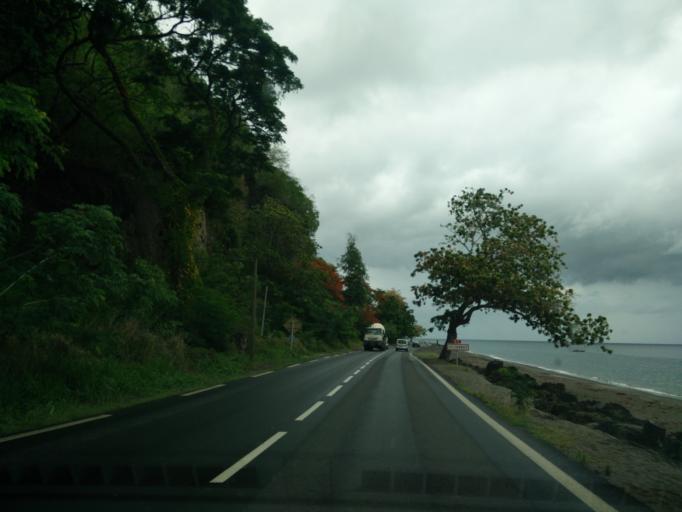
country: MQ
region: Martinique
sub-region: Martinique
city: Saint-Pierre
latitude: 14.7177
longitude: -61.1827
